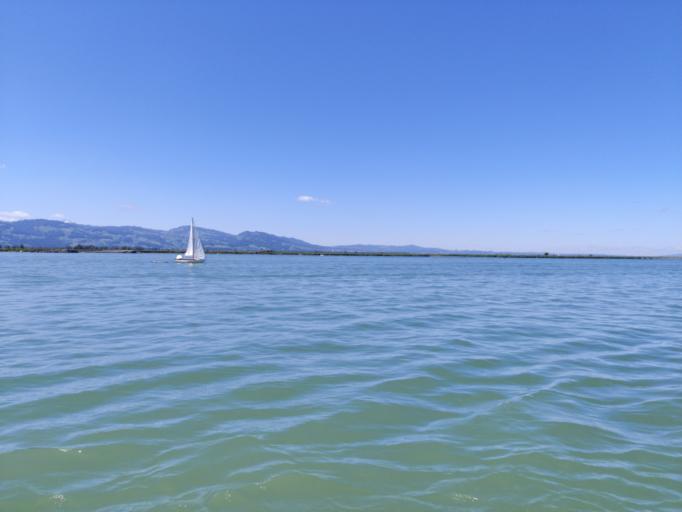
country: DE
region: Bavaria
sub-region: Swabia
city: Lindau
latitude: 47.5212
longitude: 9.6618
